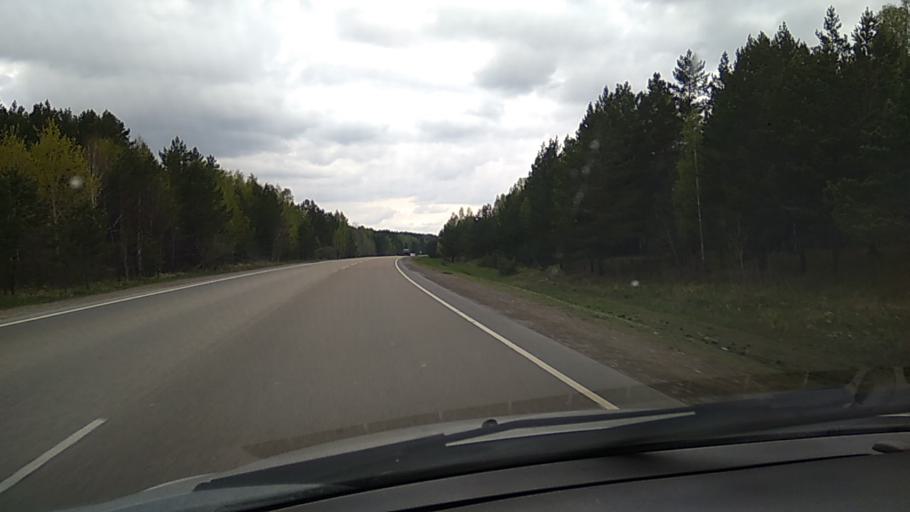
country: RU
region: Kurgan
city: Kataysk
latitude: 56.2969
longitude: 62.3915
